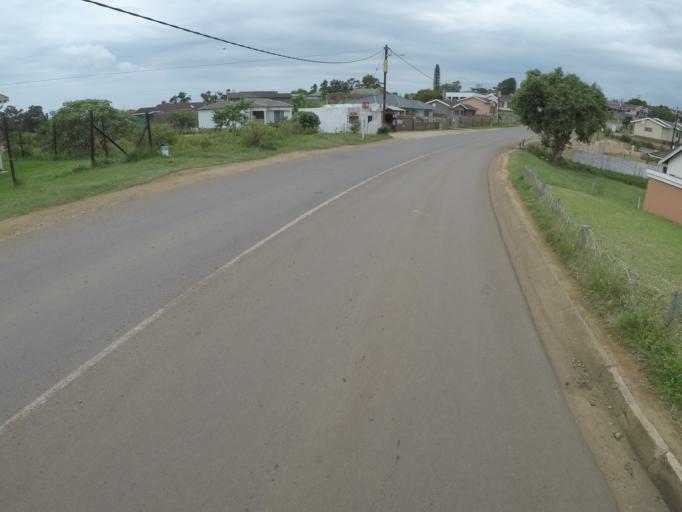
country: ZA
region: KwaZulu-Natal
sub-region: uThungulu District Municipality
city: Empangeni
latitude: -28.7851
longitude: 31.8531
